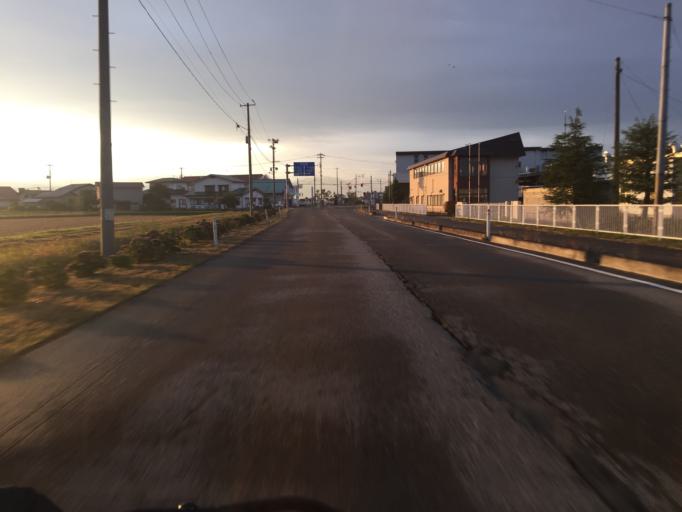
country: JP
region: Fukushima
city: Kitakata
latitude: 37.5556
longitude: 139.8914
